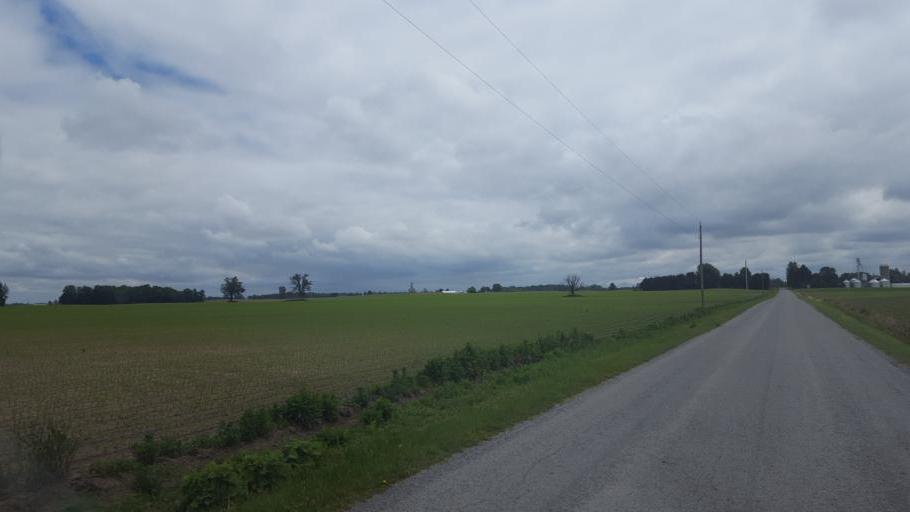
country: US
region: Ohio
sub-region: Crawford County
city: Bucyrus
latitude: 40.7753
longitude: -83.0875
